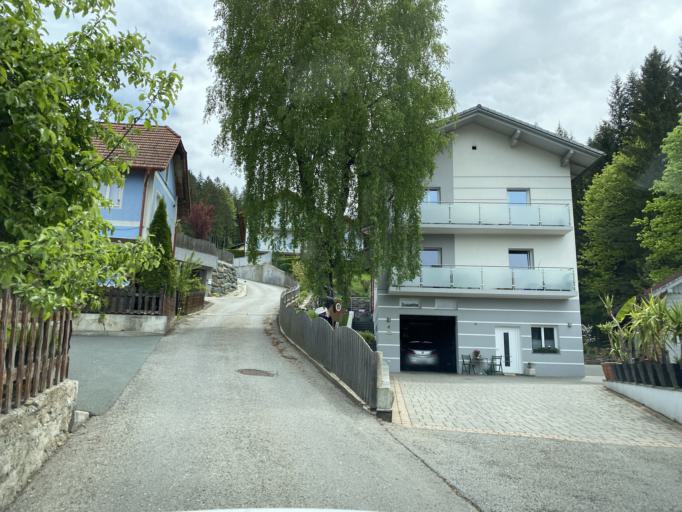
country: AT
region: Styria
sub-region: Politischer Bezirk Weiz
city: Birkfeld
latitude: 47.3525
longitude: 15.7021
